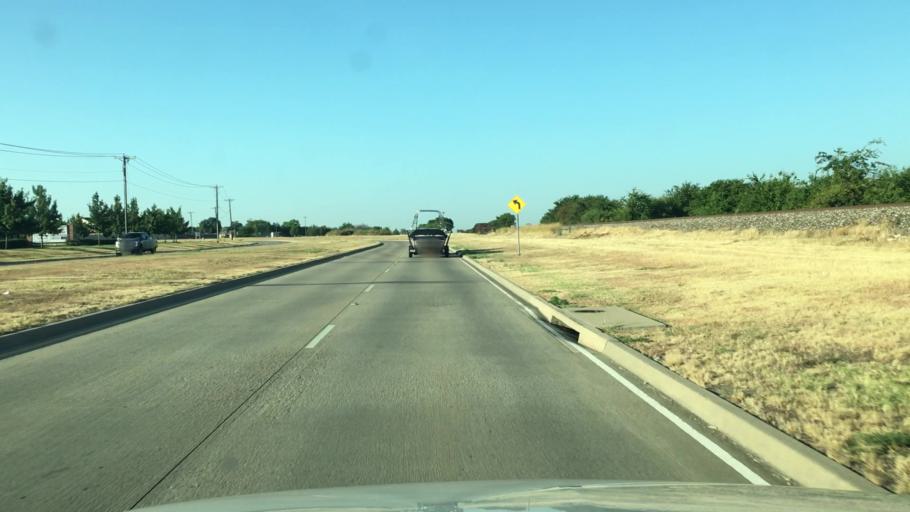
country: US
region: Texas
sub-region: Tarrant County
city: Crowley
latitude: 32.5473
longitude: -97.3657
